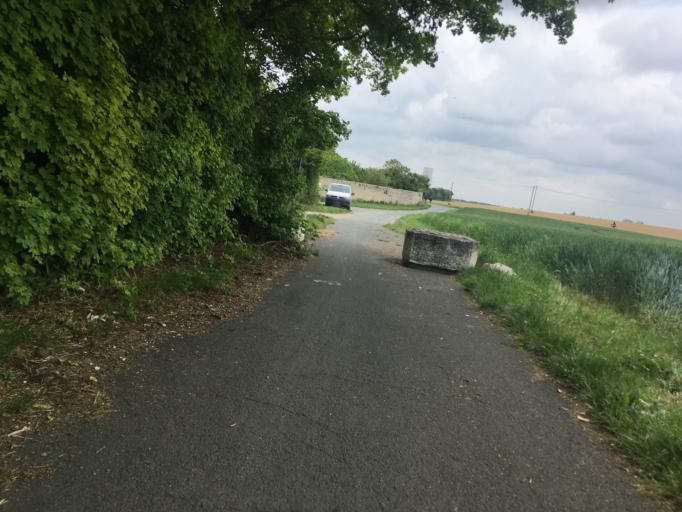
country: FR
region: Poitou-Charentes
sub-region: Departement de la Charente-Maritime
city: Aytre
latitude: 46.1464
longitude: -1.1229
